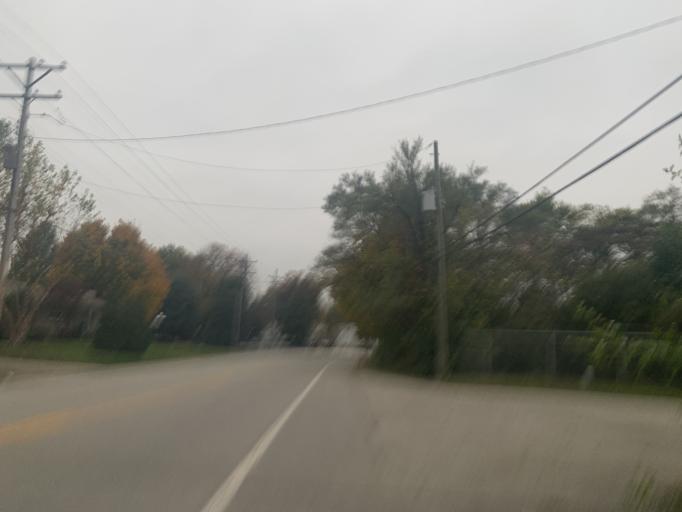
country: US
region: Kentucky
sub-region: Jefferson County
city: Shively
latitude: 38.2137
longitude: -85.8285
